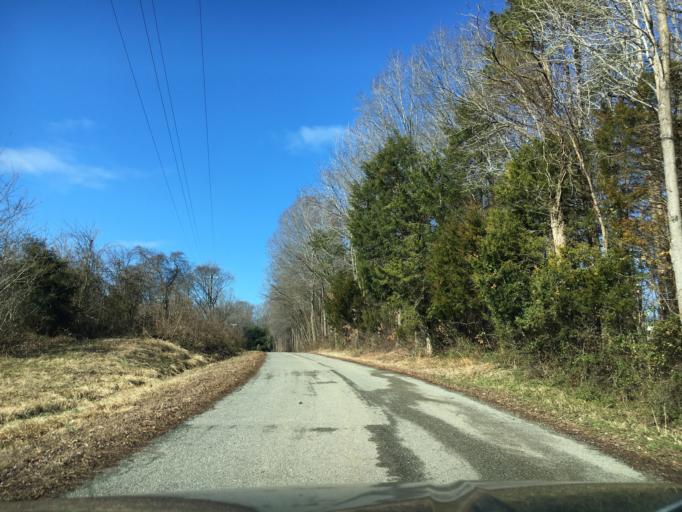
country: US
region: Virginia
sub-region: Halifax County
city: South Boston
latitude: 36.6962
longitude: -78.8825
